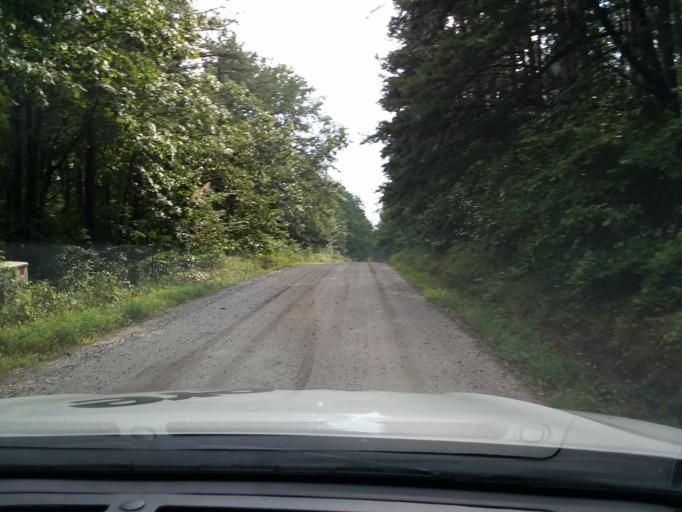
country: US
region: Georgia
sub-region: Habersham County
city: Clarkesville
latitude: 34.7127
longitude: -83.4141
